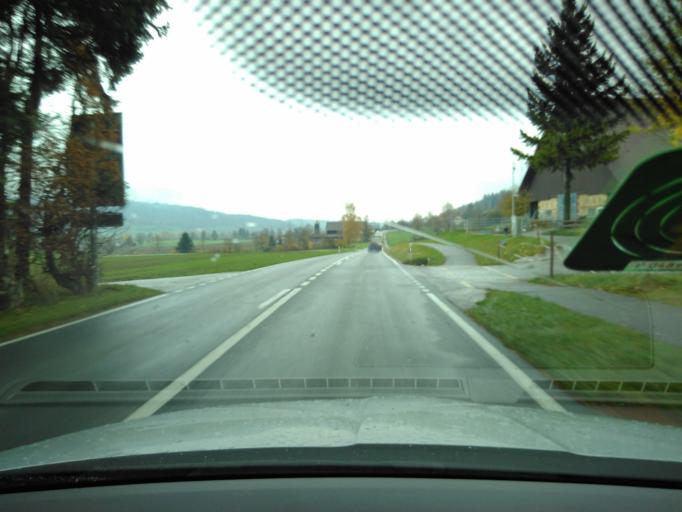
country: CH
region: Lucerne
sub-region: Sursee District
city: Triengen
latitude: 47.2483
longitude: 8.0686
